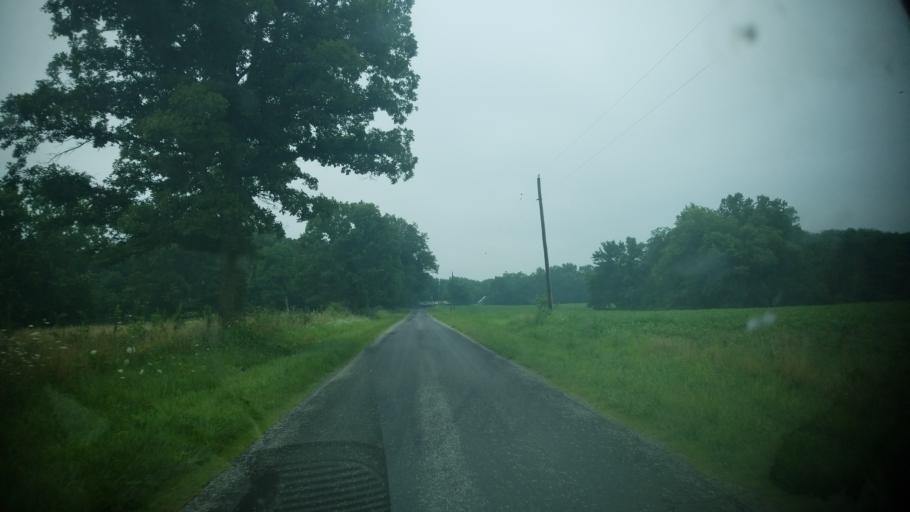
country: US
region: Illinois
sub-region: Clay County
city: Flora
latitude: 38.5770
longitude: -88.3647
